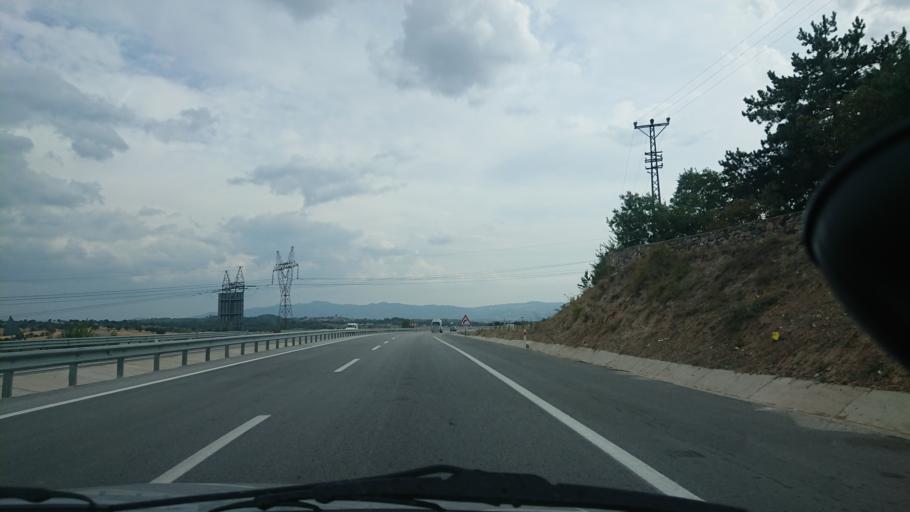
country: TR
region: Kuetahya
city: Gediz
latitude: 39.0291
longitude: 29.4164
